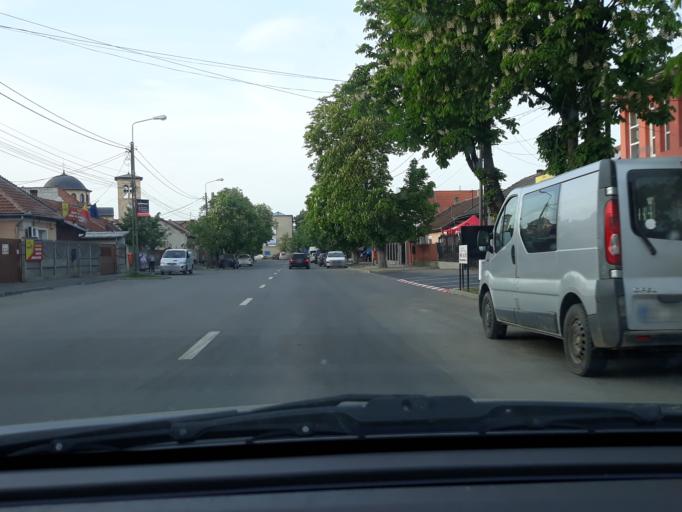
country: RO
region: Bihor
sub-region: Comuna Biharea
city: Oradea
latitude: 47.0416
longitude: 21.9556
